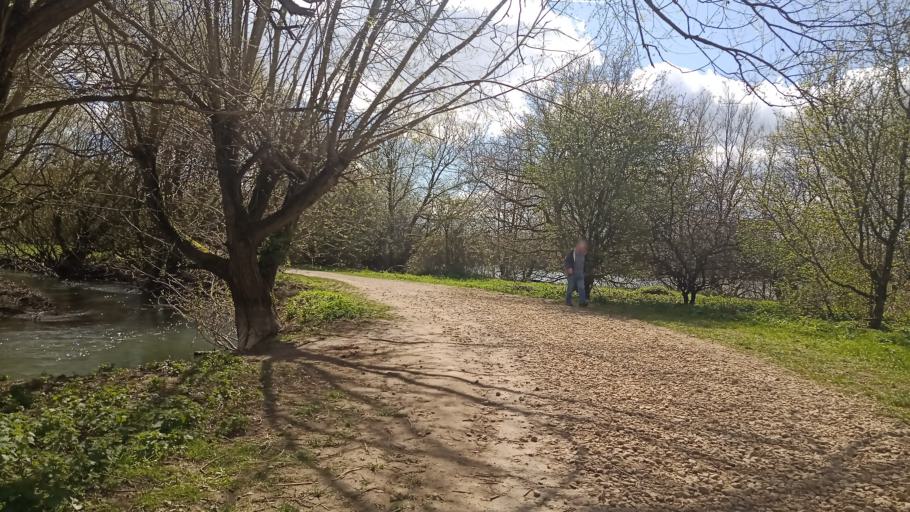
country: GB
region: England
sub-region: Oxfordshire
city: Ducklington
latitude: 51.7741
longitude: -1.4804
